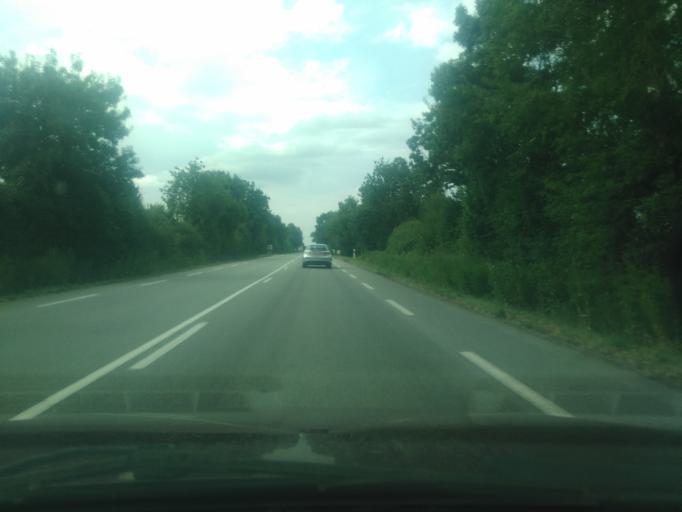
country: FR
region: Pays de la Loire
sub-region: Departement de la Vendee
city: Chantonnay
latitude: 46.7147
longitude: -1.0688
